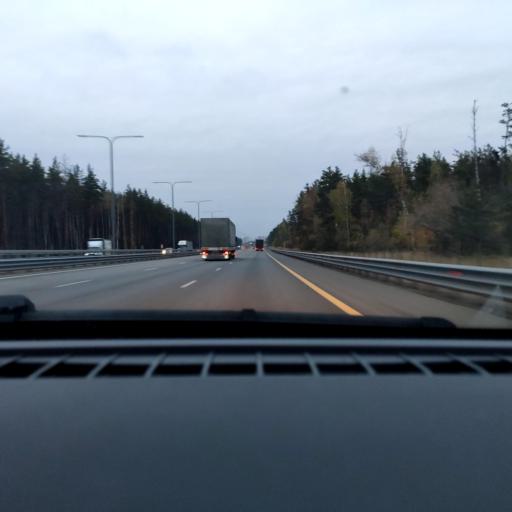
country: RU
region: Voronezj
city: Somovo
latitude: 51.7137
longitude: 39.3087
